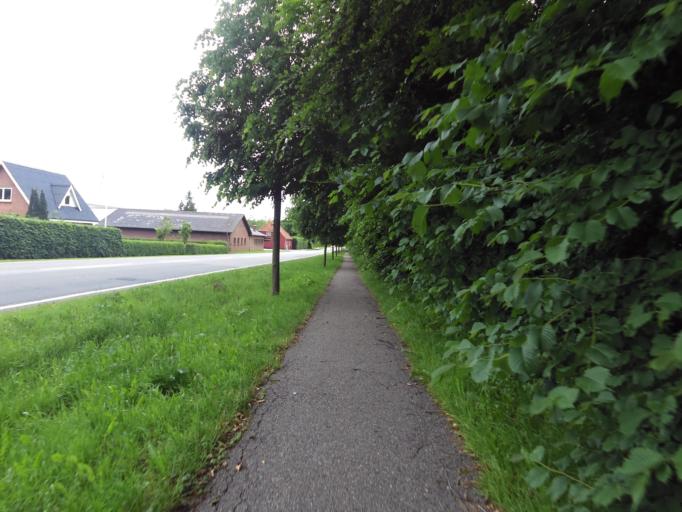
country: DK
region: South Denmark
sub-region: Haderslev Kommune
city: Gram
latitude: 55.3008
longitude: 9.0601
